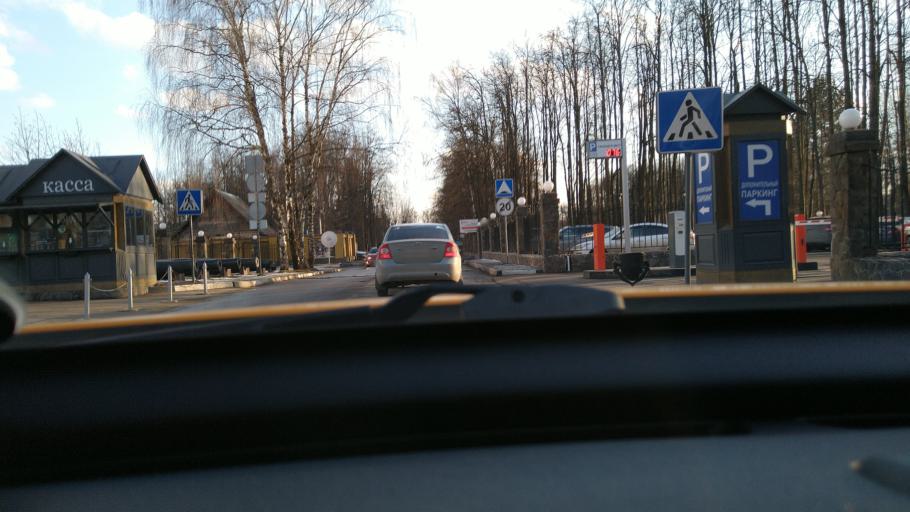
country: RU
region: Moskovskaya
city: Arkhangel'skoye
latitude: 55.7960
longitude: 37.2956
